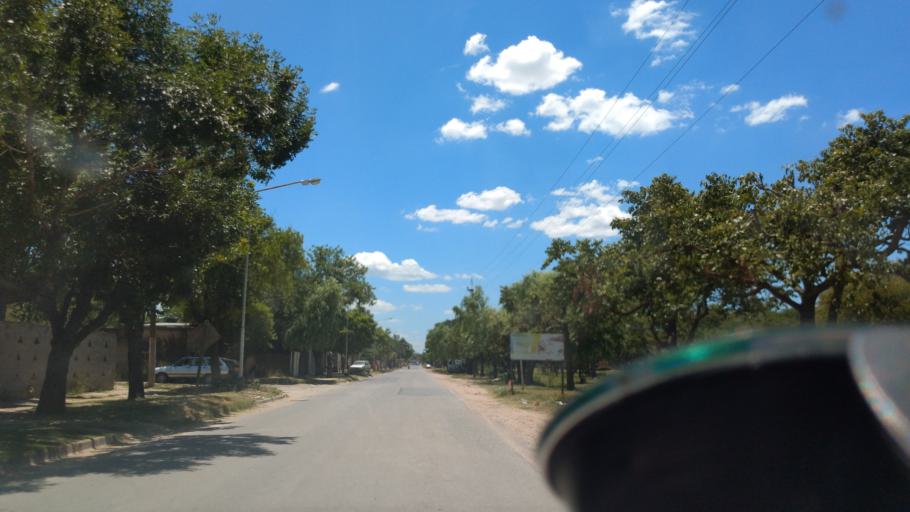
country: AR
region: Santa Fe
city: Laguna Paiva
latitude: -31.3132
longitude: -60.6585
